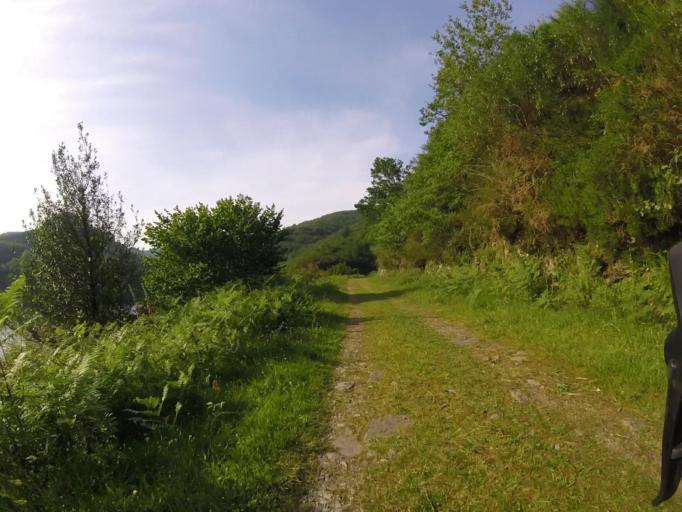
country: ES
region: Navarre
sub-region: Provincia de Navarra
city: Arano
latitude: 43.2278
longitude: -1.8658
